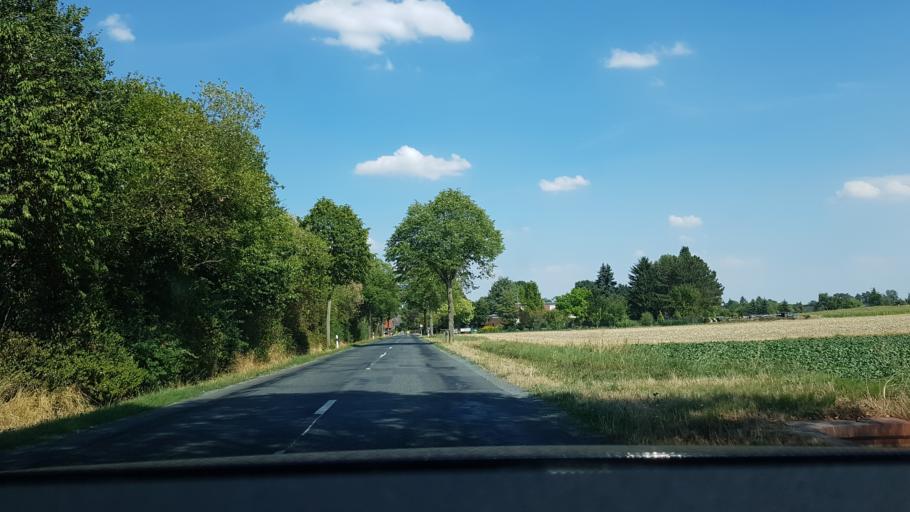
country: DE
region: Lower Saxony
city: Isenbuttel
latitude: 52.4356
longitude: 10.5669
